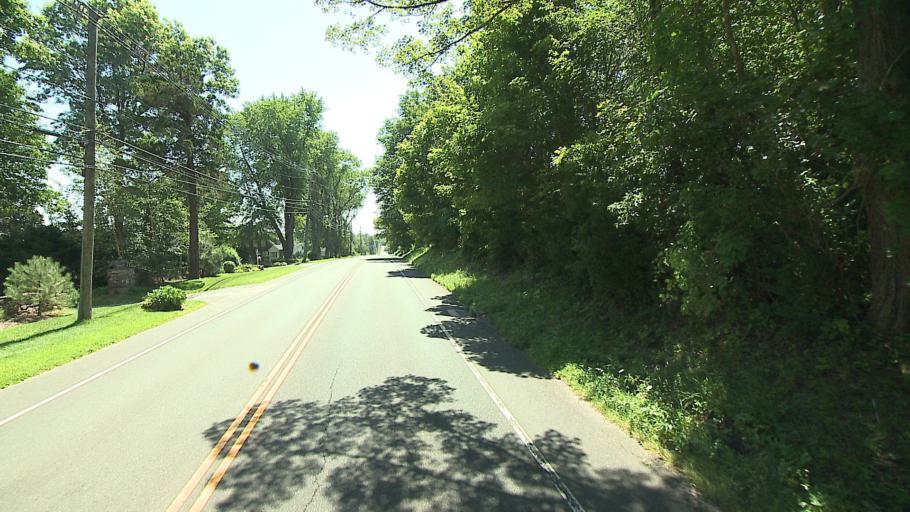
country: US
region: Connecticut
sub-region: Litchfield County
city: Litchfield
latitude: 41.8330
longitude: -73.2668
